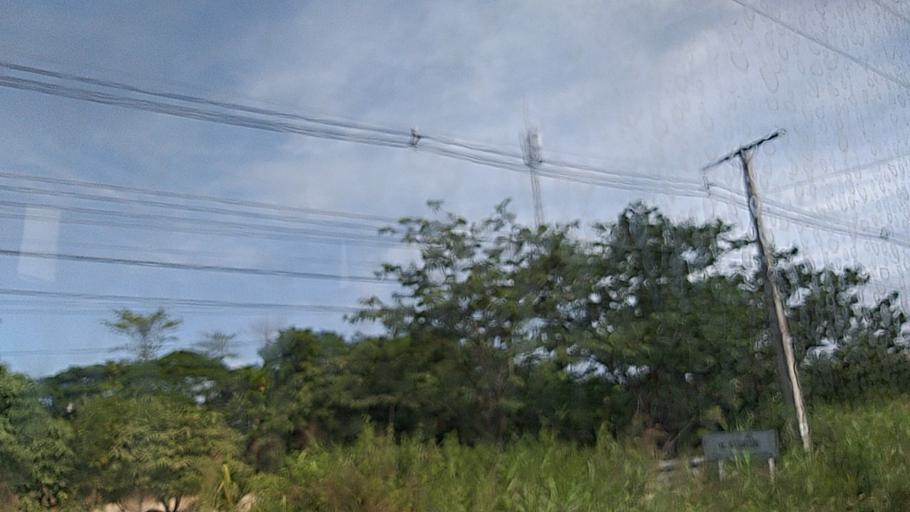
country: TH
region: Maha Sarakham
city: Chiang Yuen
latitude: 16.4428
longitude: 102.9885
